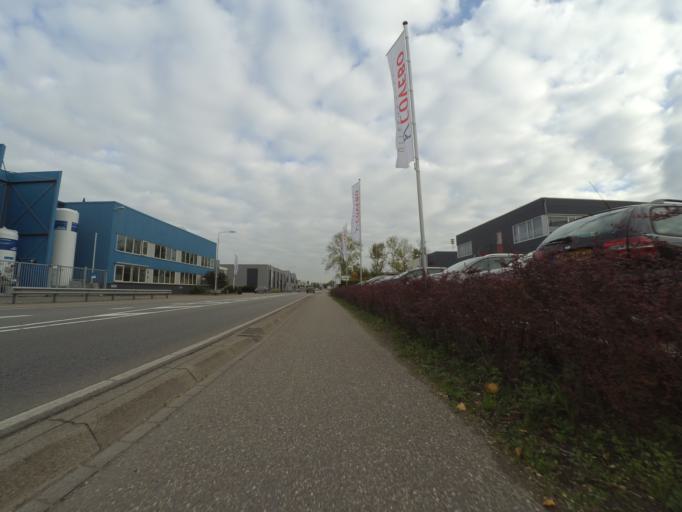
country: NL
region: Gelderland
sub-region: Gemeente Nijkerk
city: Nijkerk
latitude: 52.2339
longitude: 5.4815
